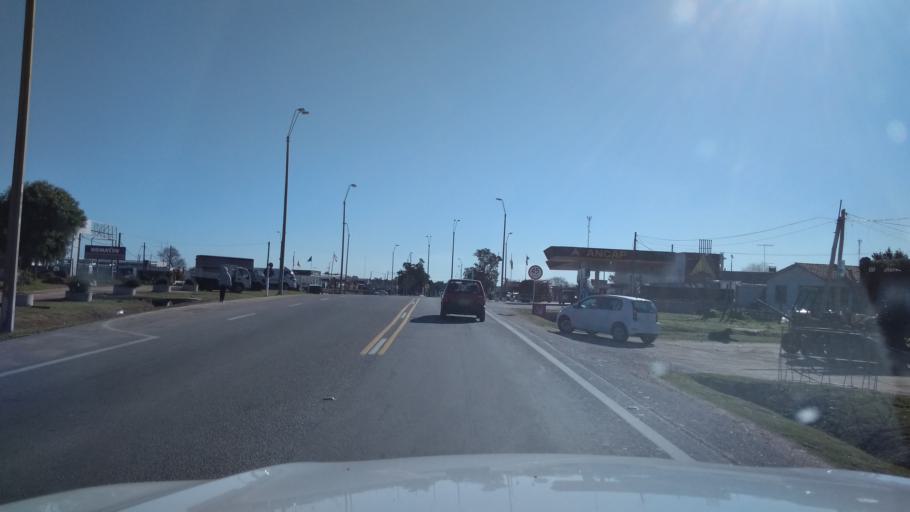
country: UY
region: Canelones
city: San Jacinto
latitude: -34.5479
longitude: -55.8719
